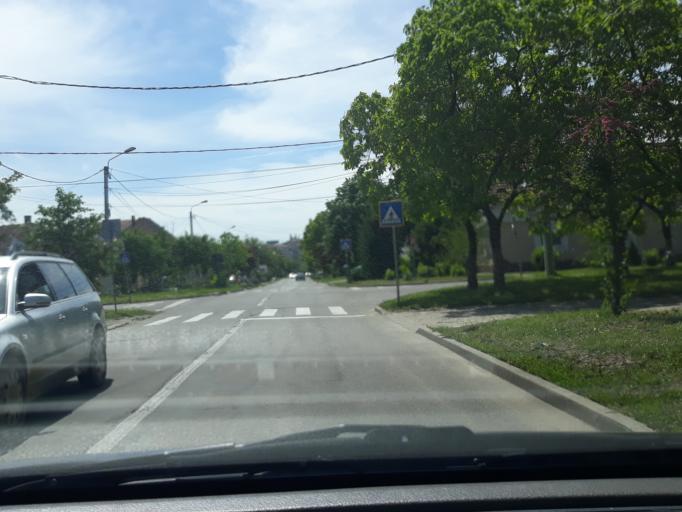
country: RO
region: Bihor
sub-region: Comuna Biharea
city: Oradea
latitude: 47.0595
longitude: 21.9060
